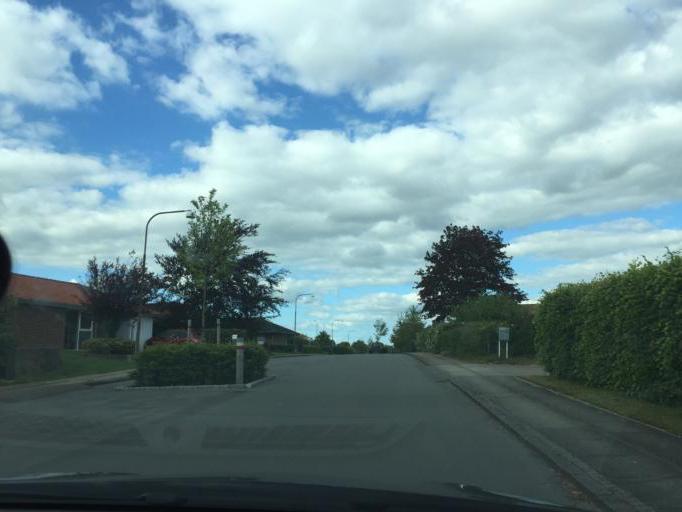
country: DK
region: South Denmark
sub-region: Odense Kommune
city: Bellinge
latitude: 55.3489
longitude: 10.3462
